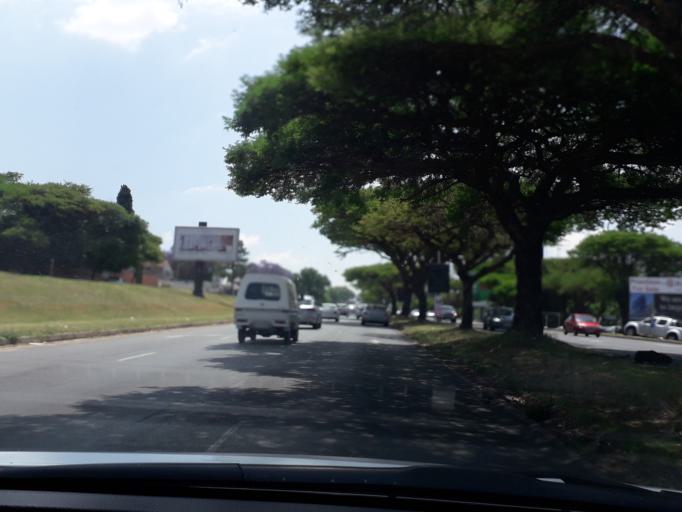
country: ZA
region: Gauteng
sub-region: City of Johannesburg Metropolitan Municipality
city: Johannesburg
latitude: -26.0813
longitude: 28.0250
